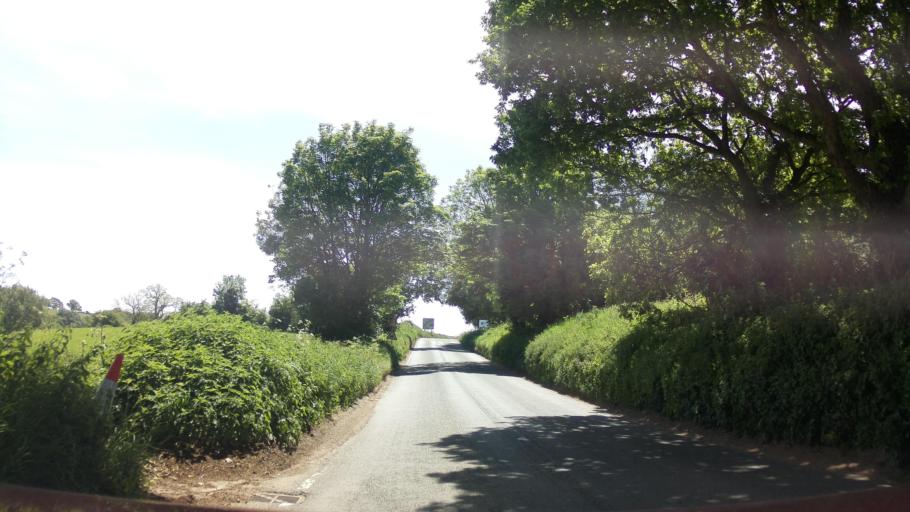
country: GB
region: England
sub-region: Devon
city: Newton Poppleford
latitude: 50.6682
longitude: -3.3075
